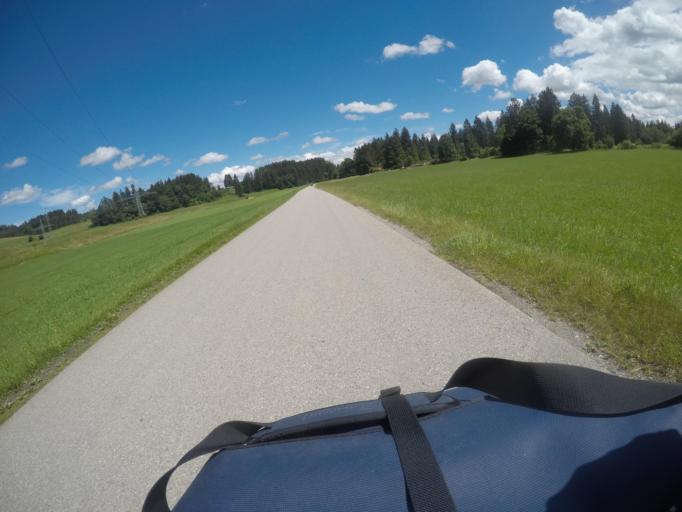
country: DE
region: Bavaria
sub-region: Upper Bavaria
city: Prem
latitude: 47.6799
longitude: 10.7891
